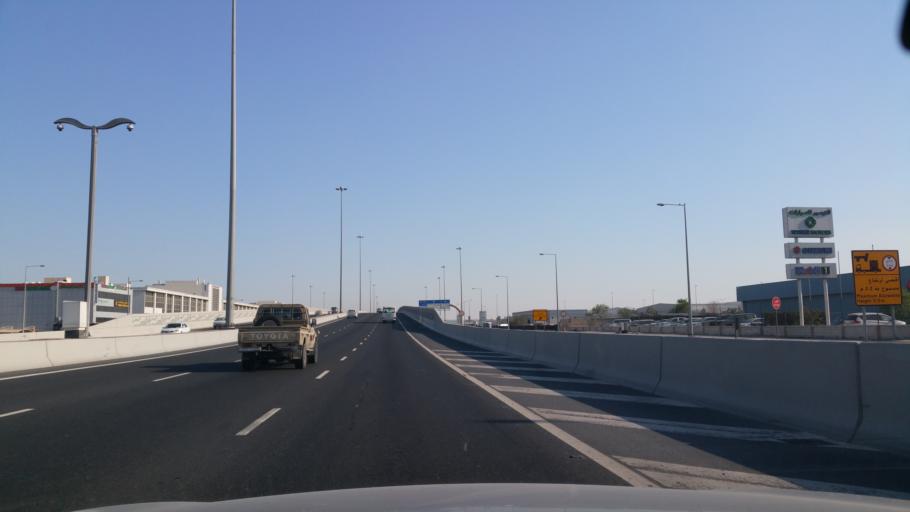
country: QA
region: Baladiyat ar Rayyan
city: Ar Rayyan
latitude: 25.2062
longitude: 51.4455
